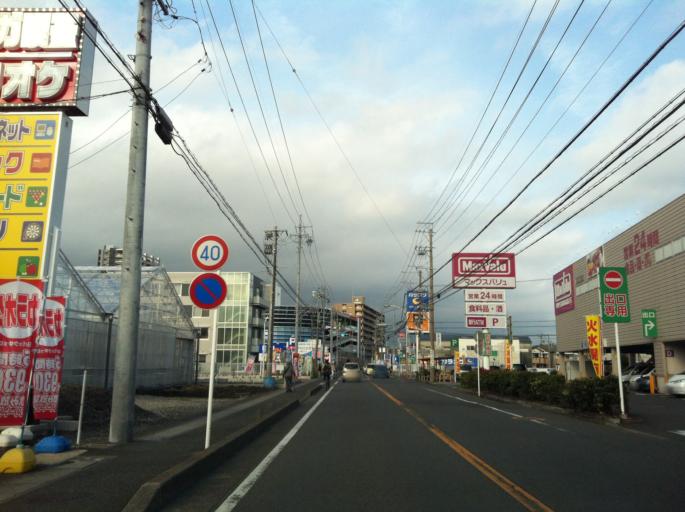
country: JP
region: Shizuoka
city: Shizuoka-shi
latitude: 34.9810
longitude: 138.4150
